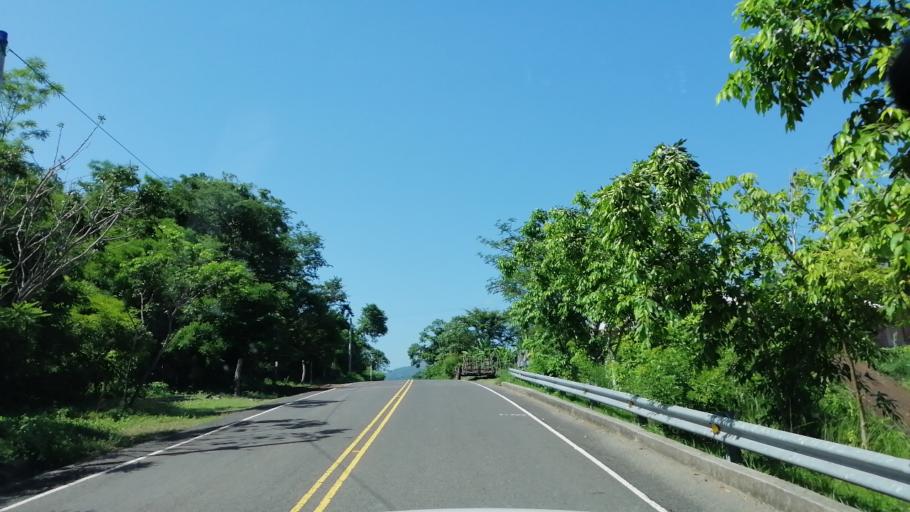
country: HN
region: Lempira
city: La Virtud
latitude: 13.9735
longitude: -88.7637
